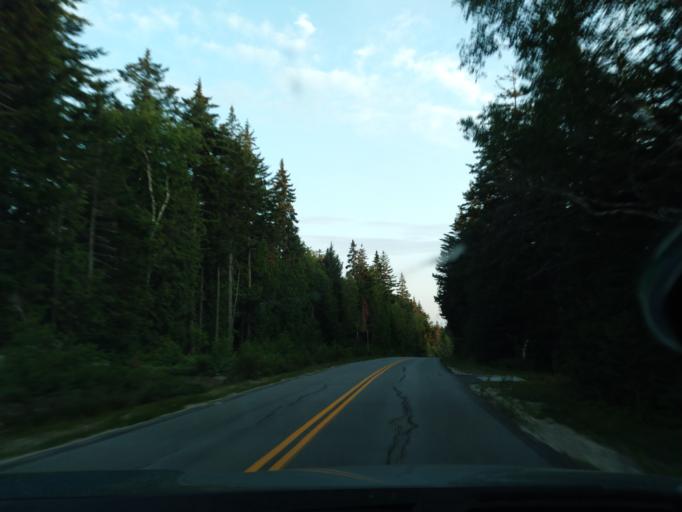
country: US
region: Maine
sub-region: Hancock County
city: Gouldsboro
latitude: 44.3797
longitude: -68.0684
